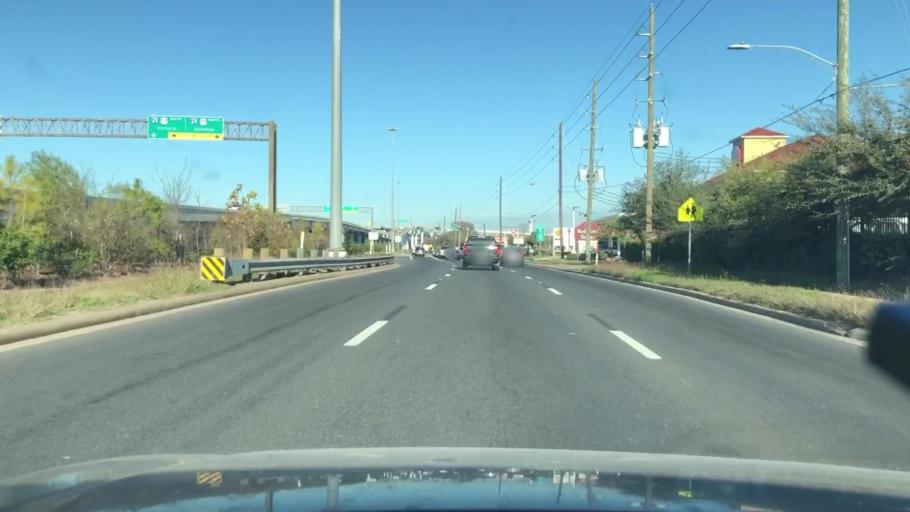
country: US
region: Texas
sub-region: Fort Bend County
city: Missouri City
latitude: 29.6526
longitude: -95.5484
